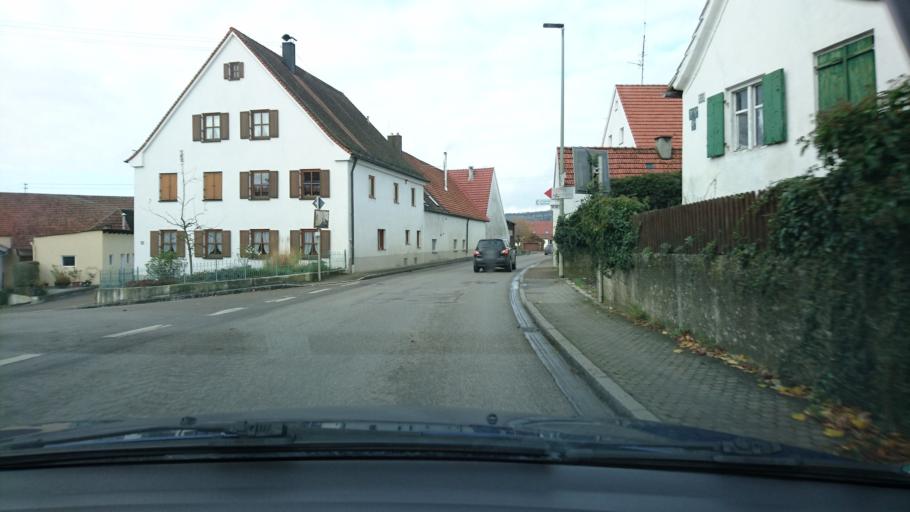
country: DE
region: Bavaria
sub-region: Swabia
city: Tapfheim
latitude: 48.7074
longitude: 10.6688
